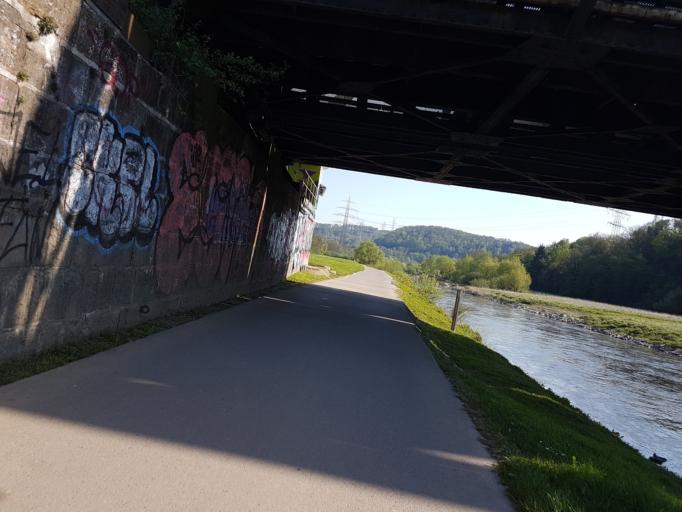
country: DE
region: North Rhine-Westphalia
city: Hattingen
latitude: 51.4002
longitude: 7.1619
